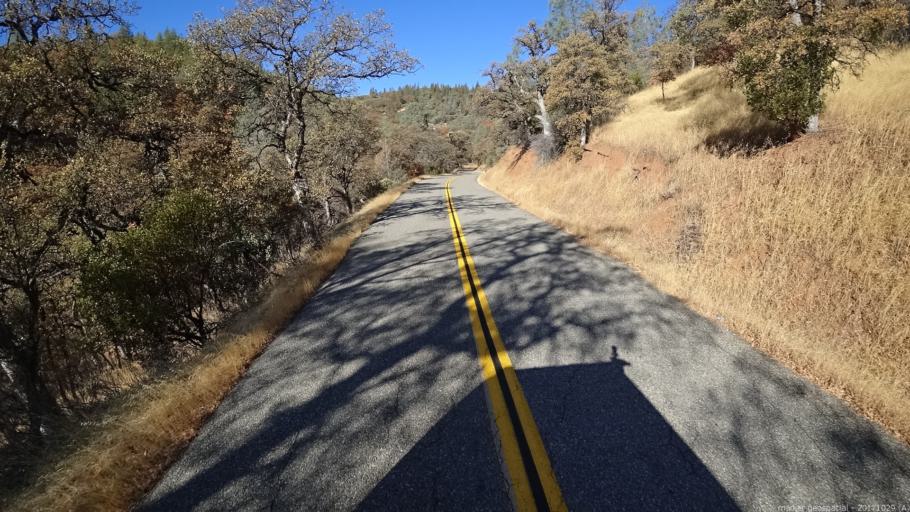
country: US
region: California
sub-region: Trinity County
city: Lewiston
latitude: 40.3693
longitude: -122.8494
